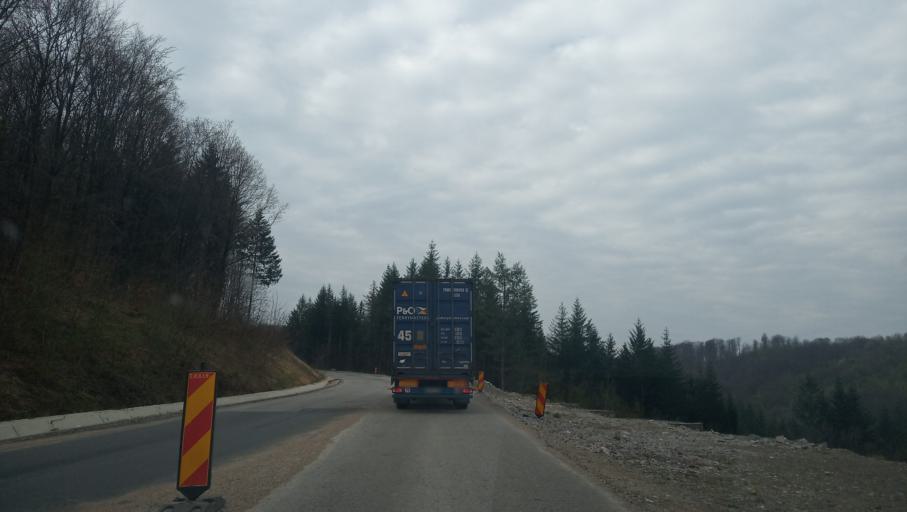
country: RO
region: Bihor
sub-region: Comuna Cristioru de Jos
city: Cristioru de Jos
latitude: 46.4136
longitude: 22.5364
